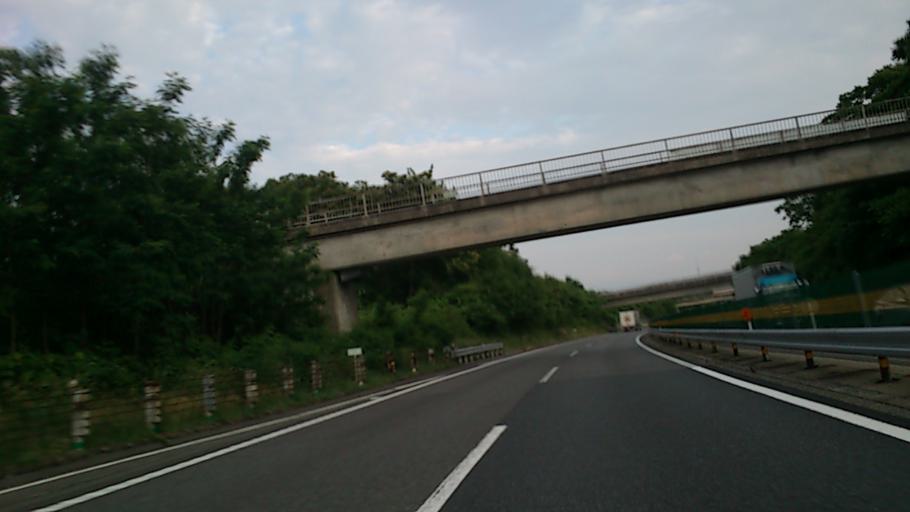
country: JP
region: Nagano
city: Ina
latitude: 35.7004
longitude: 137.9107
